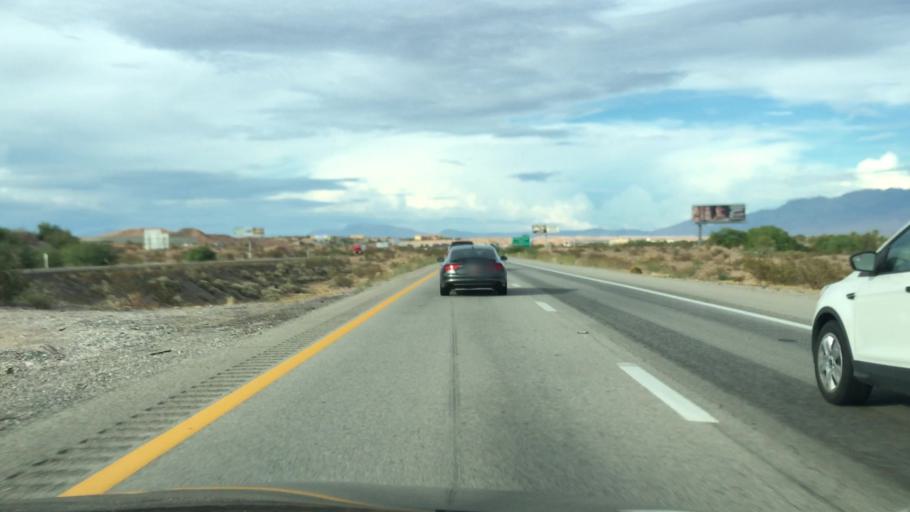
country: US
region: Nevada
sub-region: Clark County
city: Bunkerville
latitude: 36.7890
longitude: -114.1278
